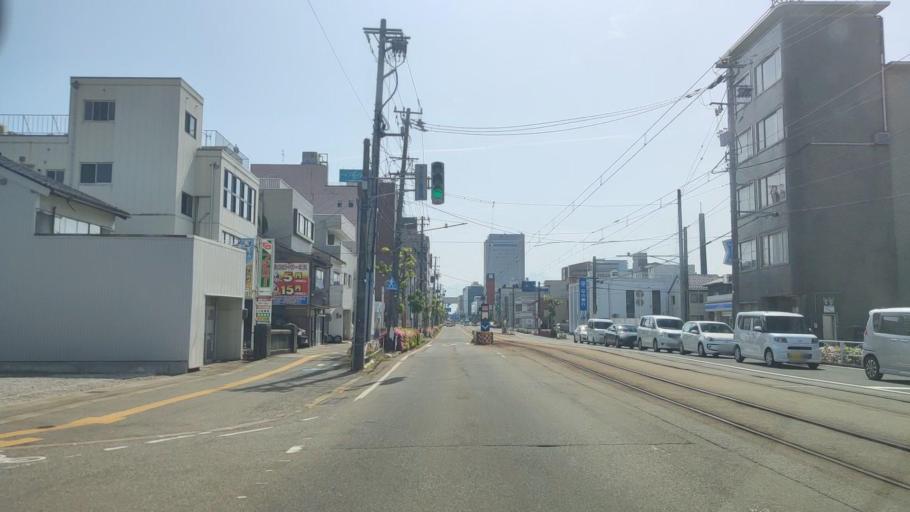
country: JP
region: Toyama
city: Toyama-shi
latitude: 36.6924
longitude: 137.2053
